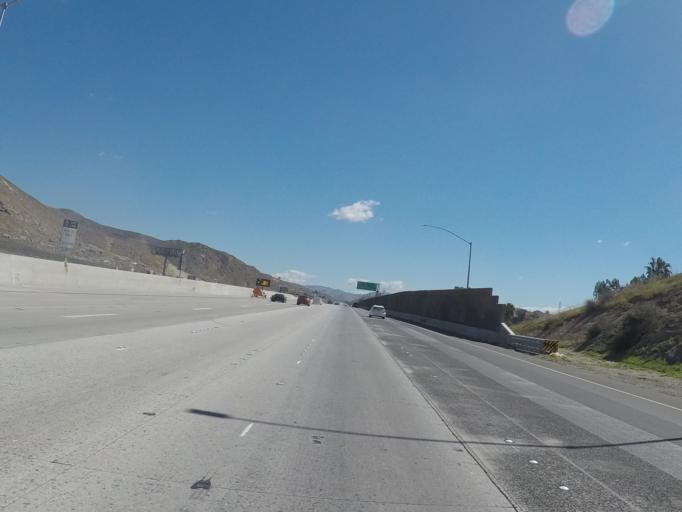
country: US
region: California
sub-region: Riverside County
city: Glen Avon
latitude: 34.0182
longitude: -117.4756
